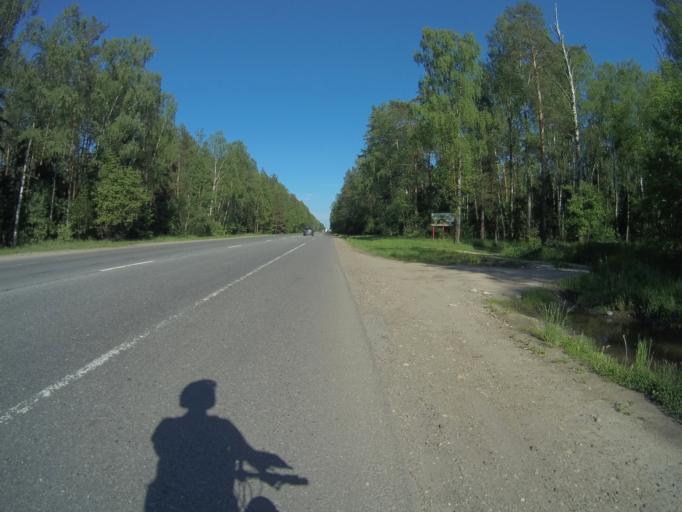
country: RU
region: Vladimir
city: Orgtrud
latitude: 56.2064
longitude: 40.7026
